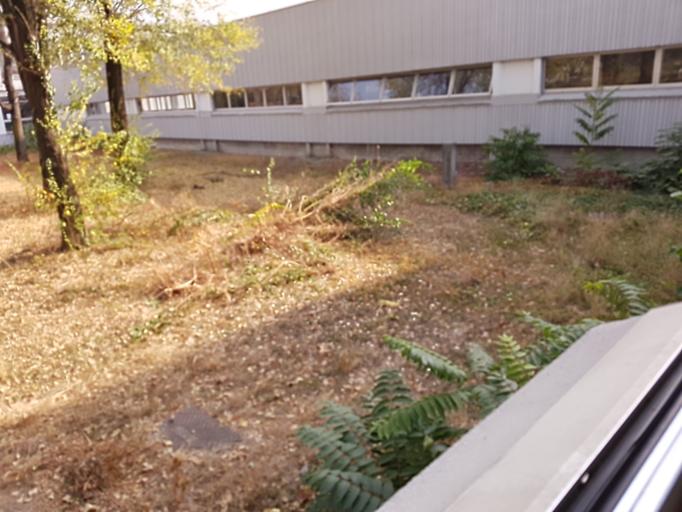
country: IT
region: Piedmont
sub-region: Provincia di Torino
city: Gerbido
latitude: 45.0506
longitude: 7.6126
